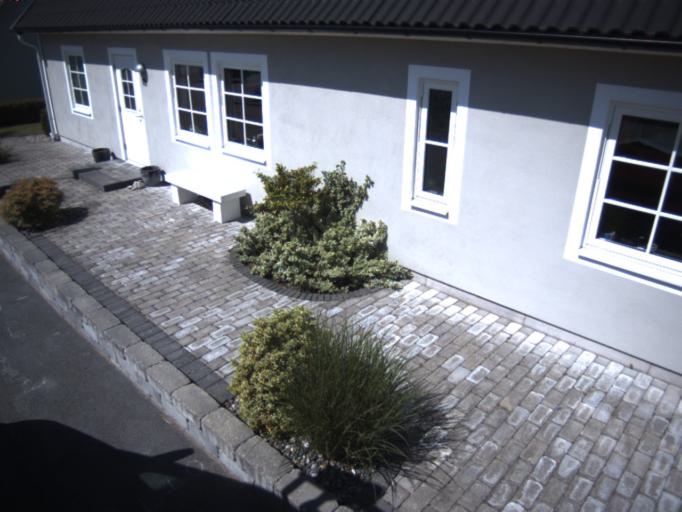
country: SE
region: Skane
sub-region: Helsingborg
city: Odakra
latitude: 56.1234
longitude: 12.6968
